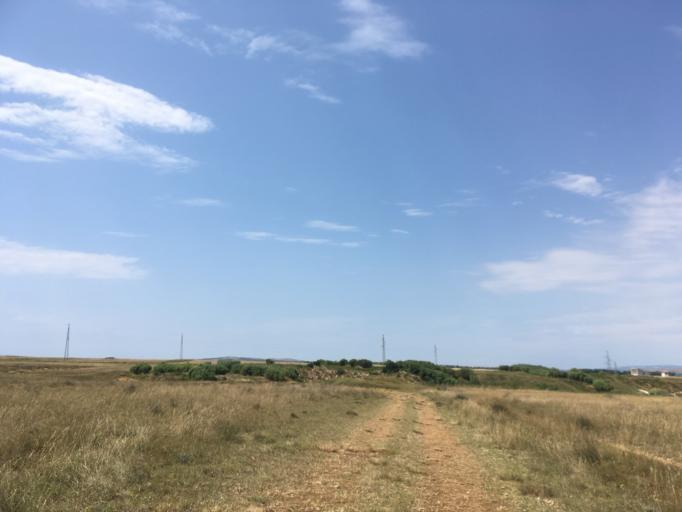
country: HR
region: Zadarska
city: Privlaka
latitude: 44.2730
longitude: 15.1486
